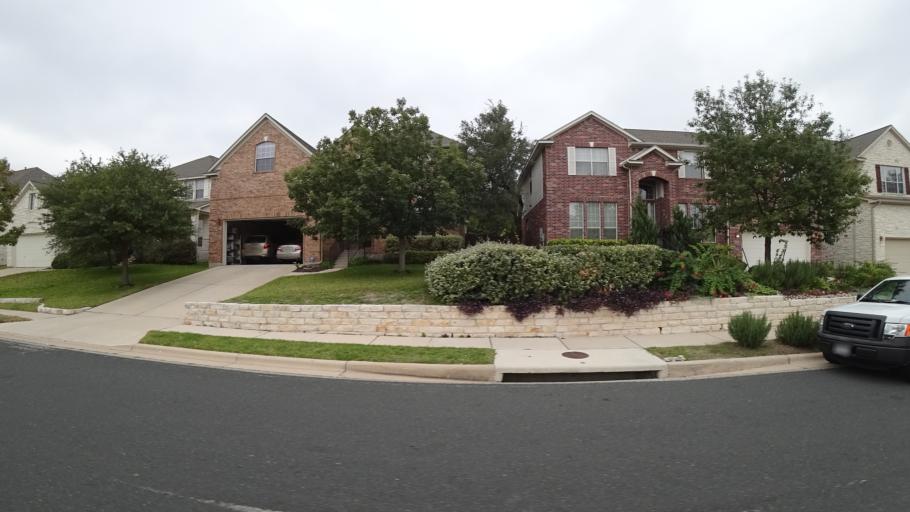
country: US
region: Texas
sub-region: Williamson County
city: Anderson Mill
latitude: 30.4334
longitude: -97.8208
